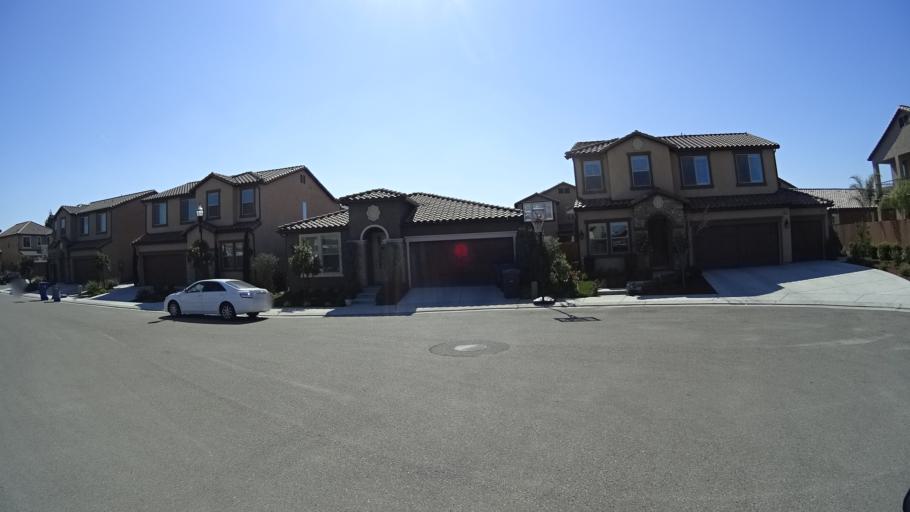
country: US
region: California
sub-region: Fresno County
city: Clovis
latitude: 36.9054
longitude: -119.7495
